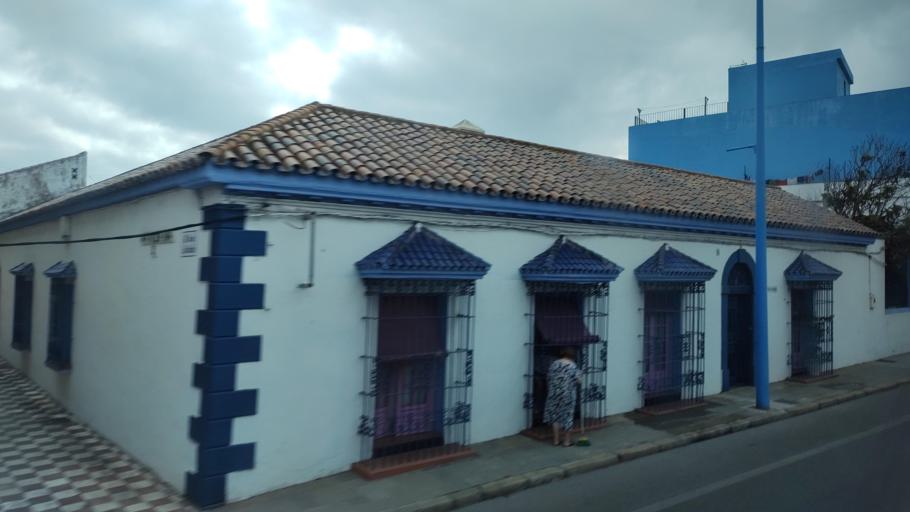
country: ES
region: Andalusia
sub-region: Provincia de Cadiz
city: La Linea de la Concepcion
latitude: 36.1783
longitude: -5.3780
